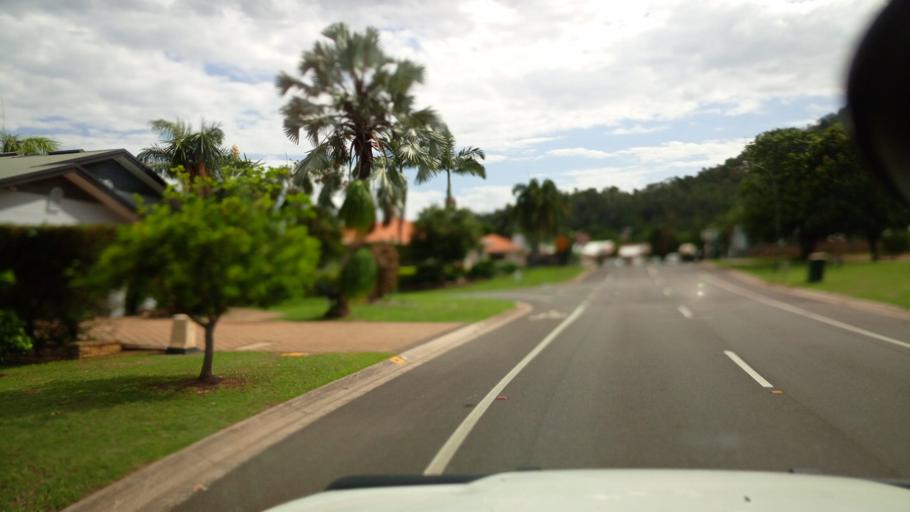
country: AU
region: Queensland
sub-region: Cairns
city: Woree
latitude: -16.9253
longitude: 145.7272
